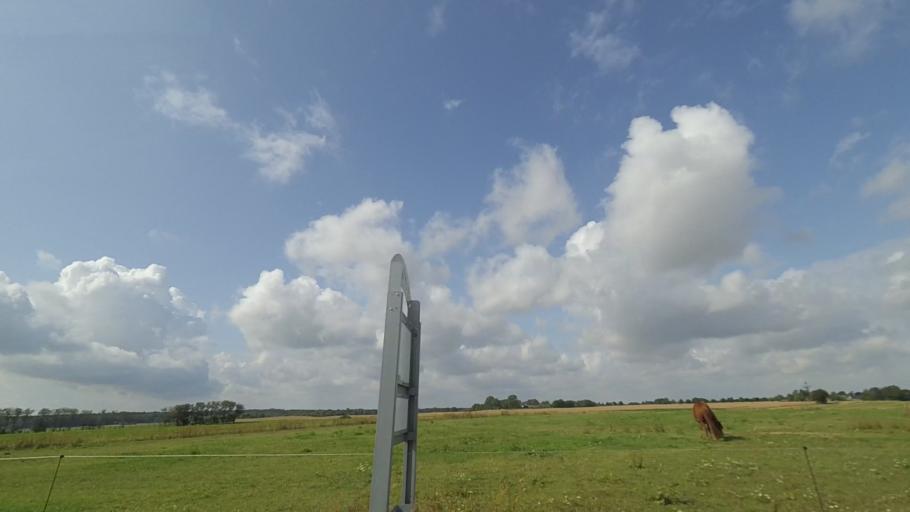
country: DK
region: Central Jutland
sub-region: Syddjurs Kommune
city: Ryomgard
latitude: 56.4746
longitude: 10.5073
